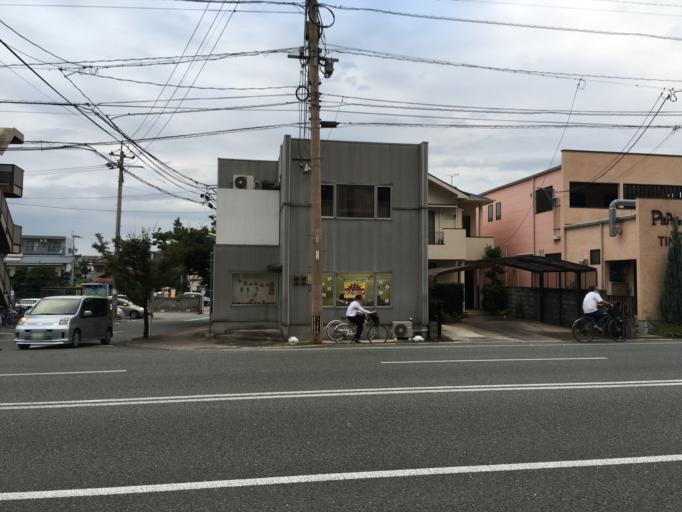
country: JP
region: Kumamoto
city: Kumamoto
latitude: 32.8066
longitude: 130.7274
